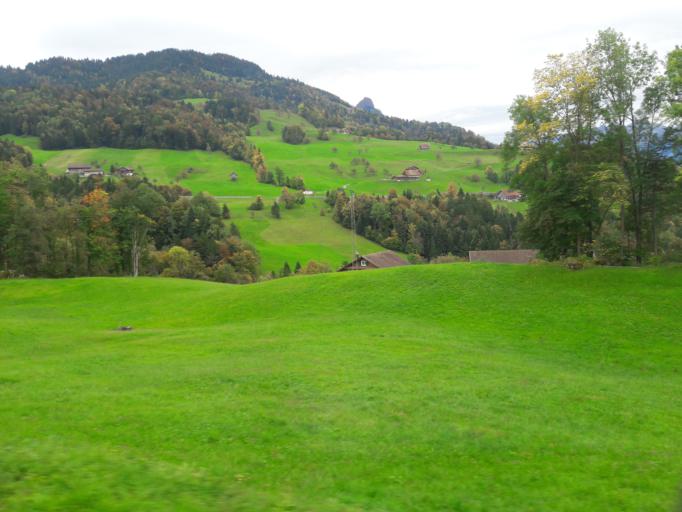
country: CH
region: Schwyz
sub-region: Bezirk Schwyz
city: Steinen
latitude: 47.0660
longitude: 8.6158
